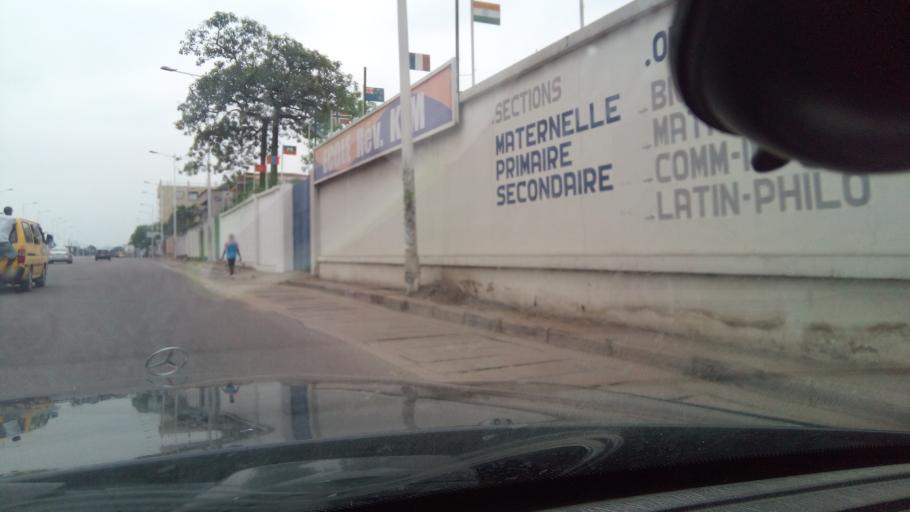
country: CD
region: Kinshasa
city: Kinshasa
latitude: -4.3325
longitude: 15.2627
